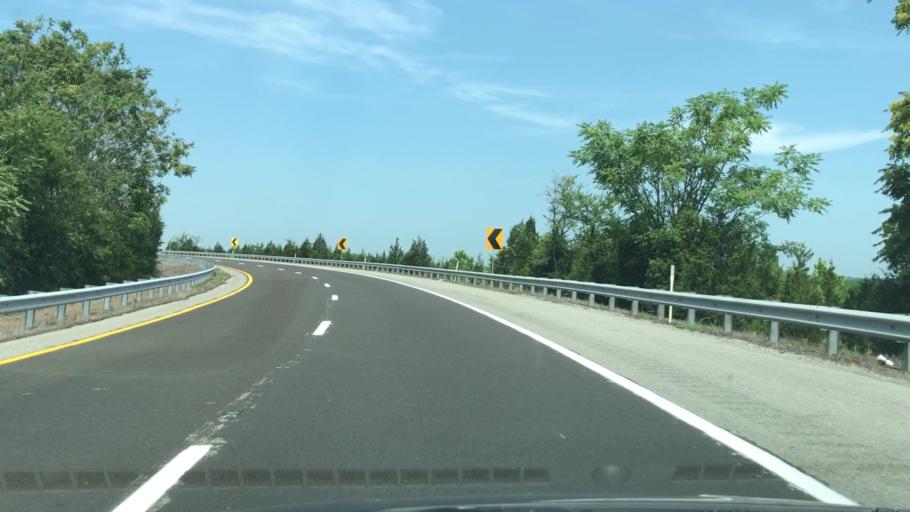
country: US
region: Tennessee
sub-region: Wilson County
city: Lebanon
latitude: 36.1857
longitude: -86.3501
